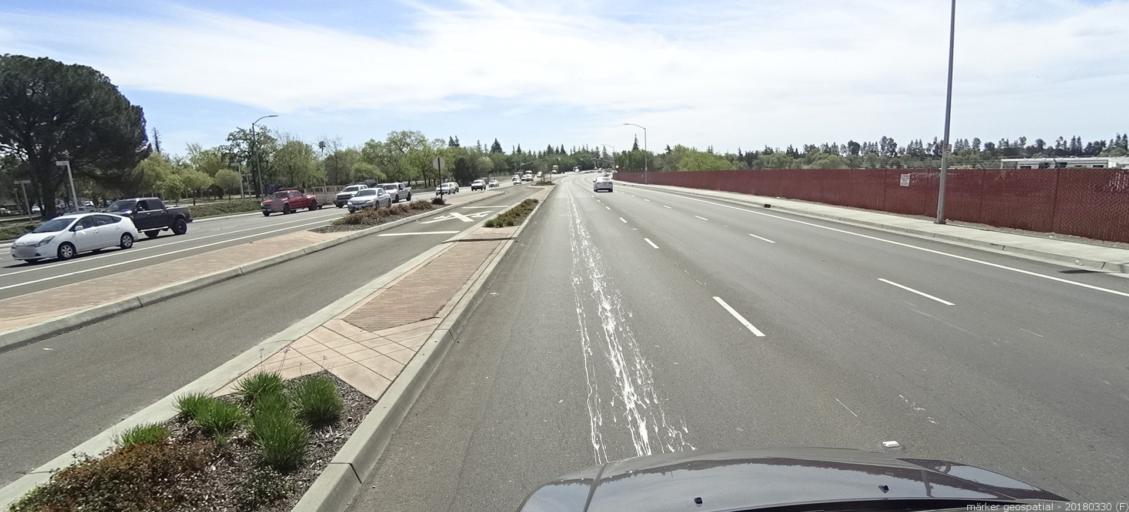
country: US
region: California
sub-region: Sacramento County
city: Rosemont
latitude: 38.5527
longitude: -121.3748
